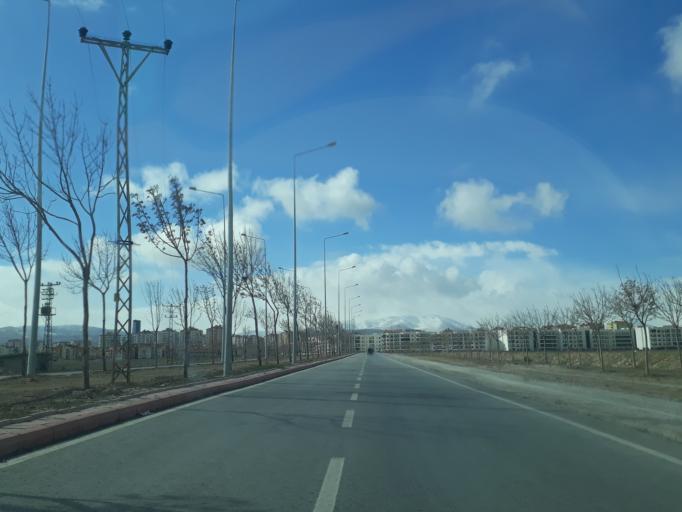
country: TR
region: Konya
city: Asagipinarbasi
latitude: 38.0058
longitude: 32.5447
